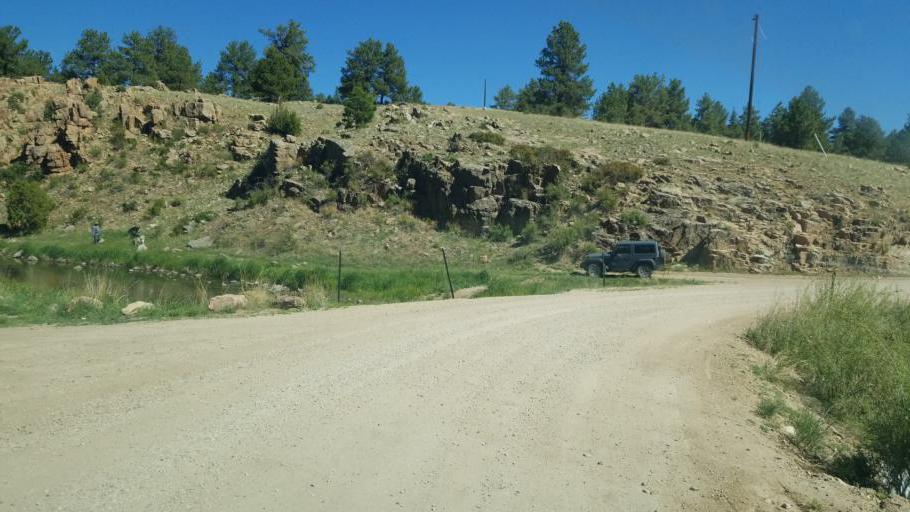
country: US
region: Colorado
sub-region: Custer County
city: Westcliffe
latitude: 38.2113
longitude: -105.4436
